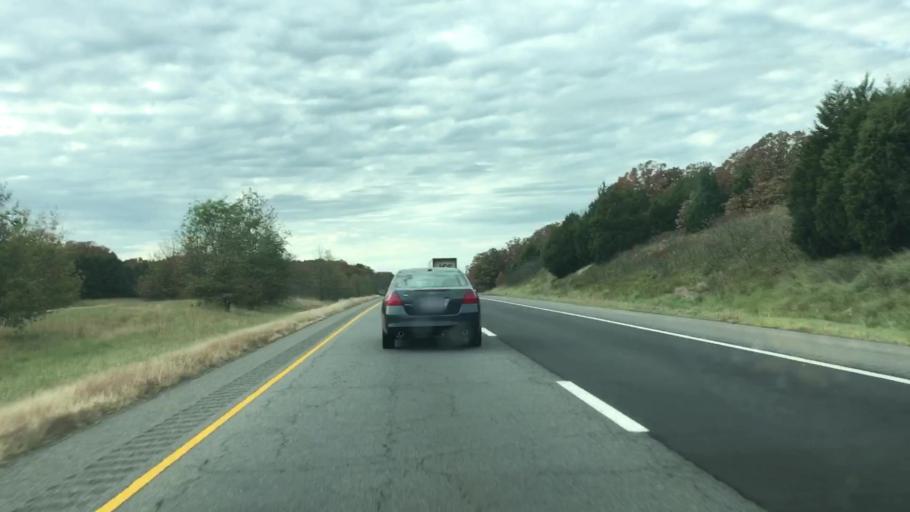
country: US
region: Arkansas
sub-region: Faulkner County
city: Conway
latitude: 35.1228
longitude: -92.4998
